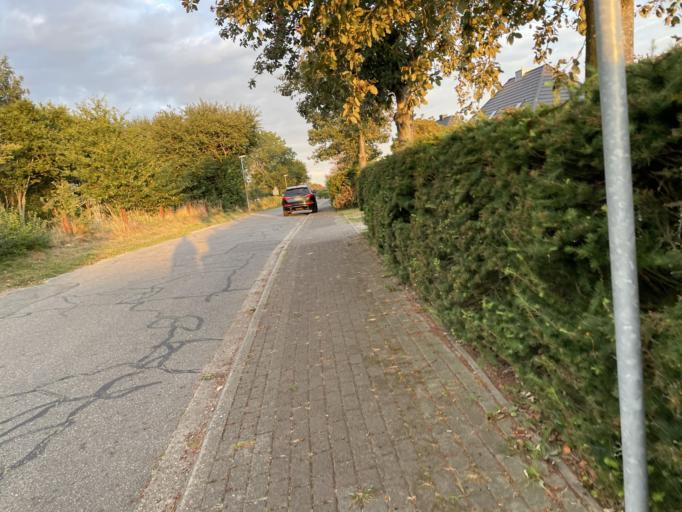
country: DE
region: Schleswig-Holstein
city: Mildstedt
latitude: 54.4785
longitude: 9.0992
